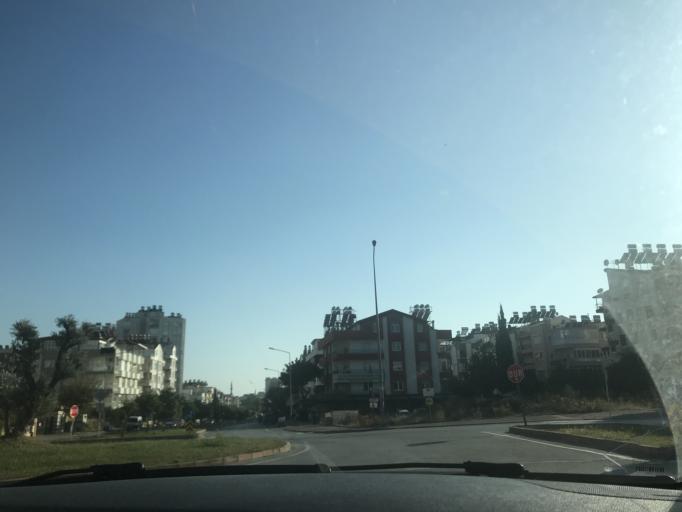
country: TR
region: Antalya
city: Antalya
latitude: 36.8883
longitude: 30.6465
